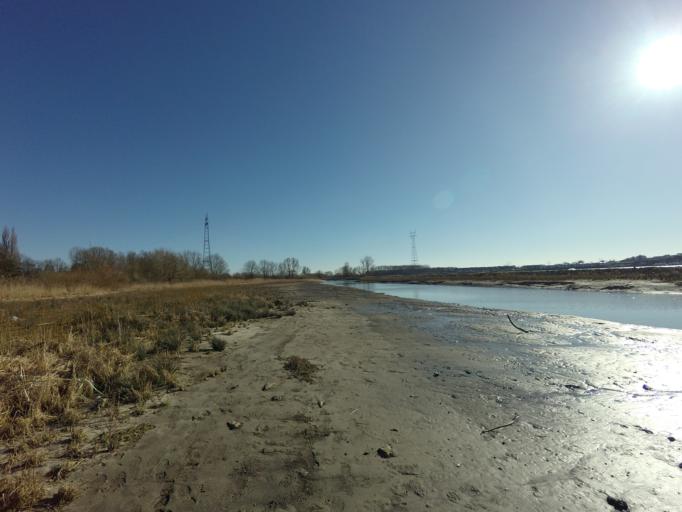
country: NL
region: South Holland
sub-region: Gemeente Krimpen aan den IJssel
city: Krimpen aan den IJssel
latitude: 51.9003
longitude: 4.5904
